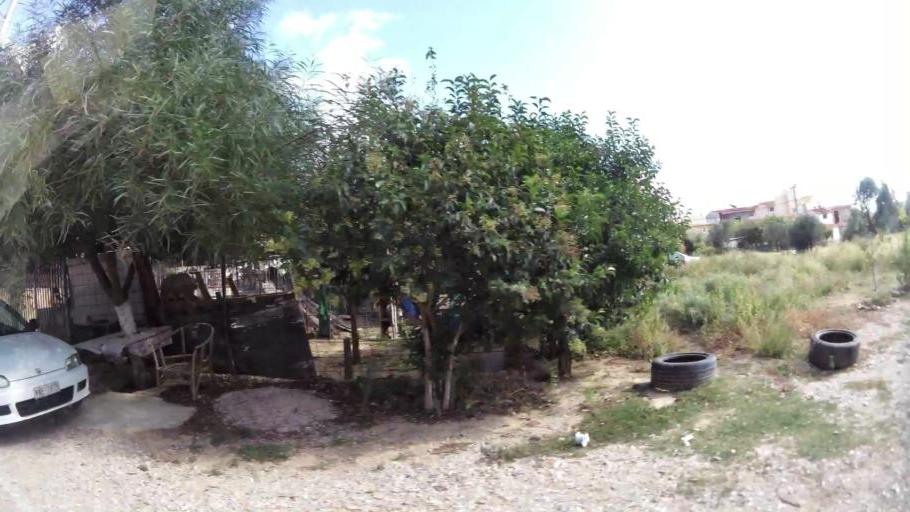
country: GR
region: Attica
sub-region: Nomarchia Anatolikis Attikis
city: Thrakomakedones
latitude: 38.1024
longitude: 23.7537
